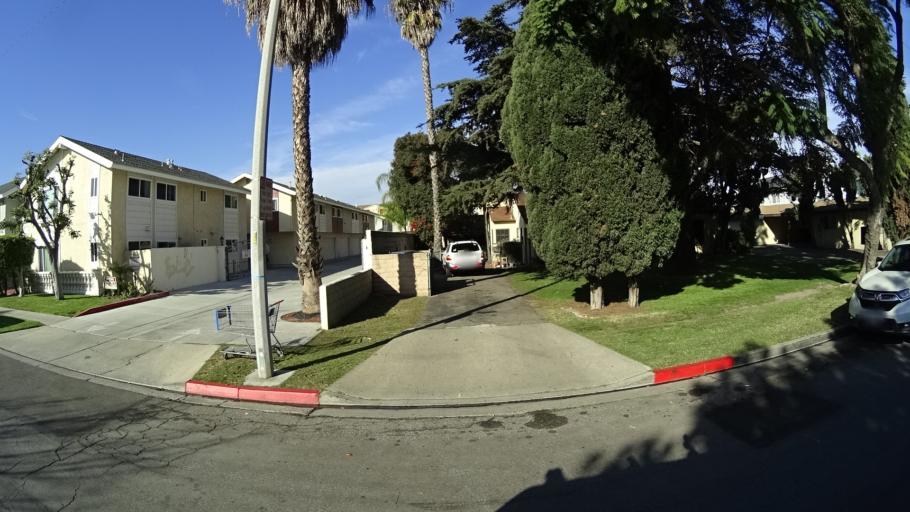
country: US
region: California
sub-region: Orange County
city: Westminster
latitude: 33.7720
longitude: -117.9877
